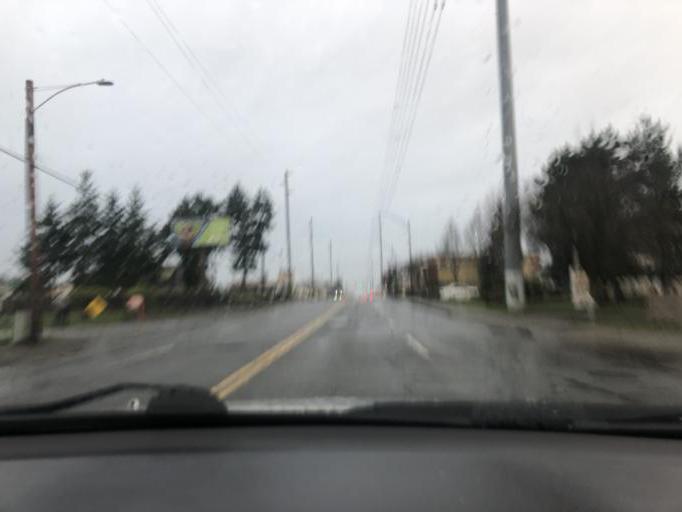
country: US
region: Washington
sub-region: Pierce County
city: Midland
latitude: 47.1918
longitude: -122.4049
